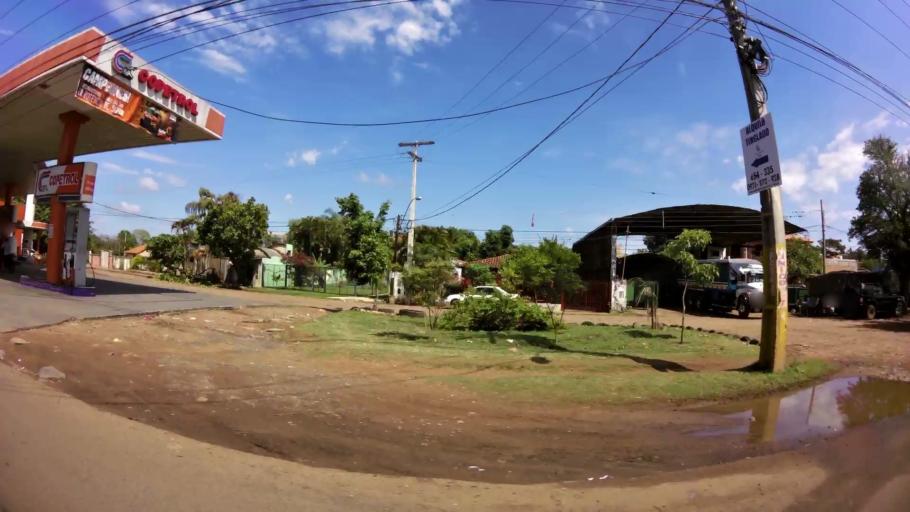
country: PY
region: Central
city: San Lorenzo
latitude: -25.2792
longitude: -57.4979
